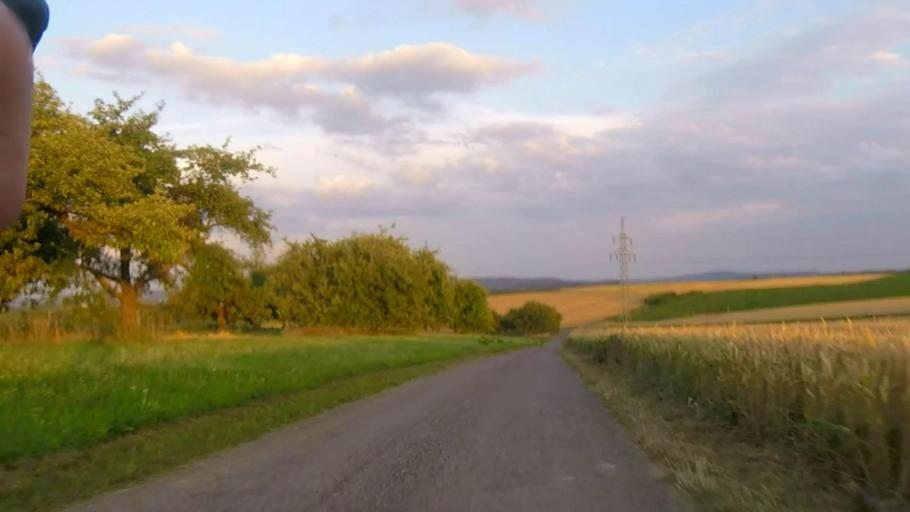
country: DE
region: Baden-Wuerttemberg
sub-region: Regierungsbezirk Stuttgart
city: Aspach
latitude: 48.9611
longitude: 9.3855
